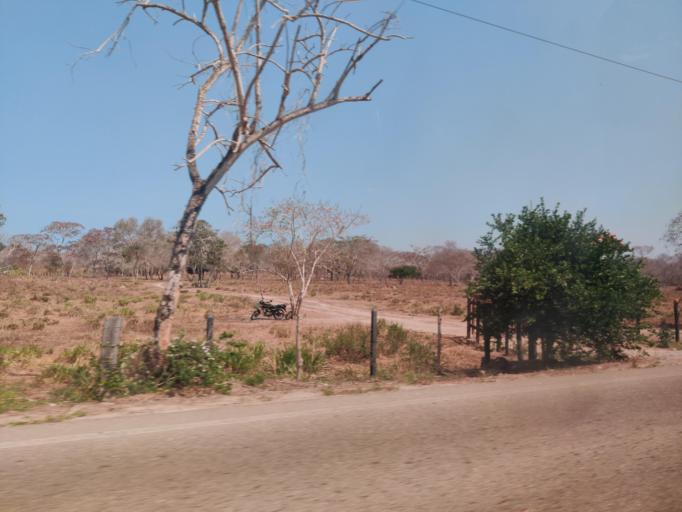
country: CO
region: Bolivar
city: Turbana
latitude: 10.2116
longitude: -75.6030
